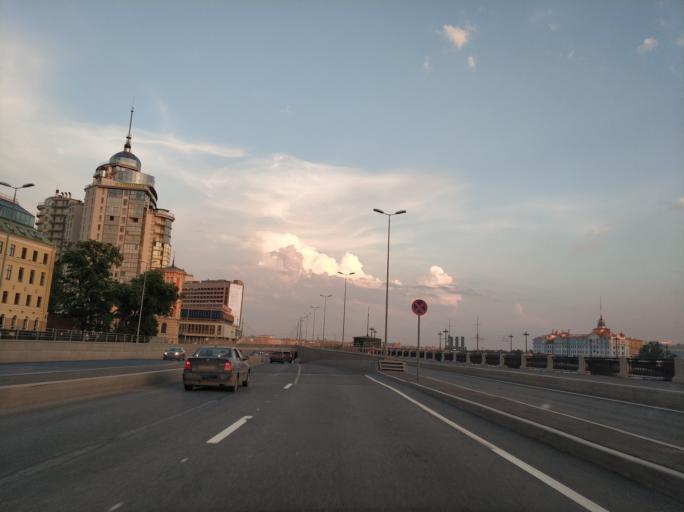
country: RU
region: Leningrad
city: Sampsonievskiy
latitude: 59.9601
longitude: 30.3383
